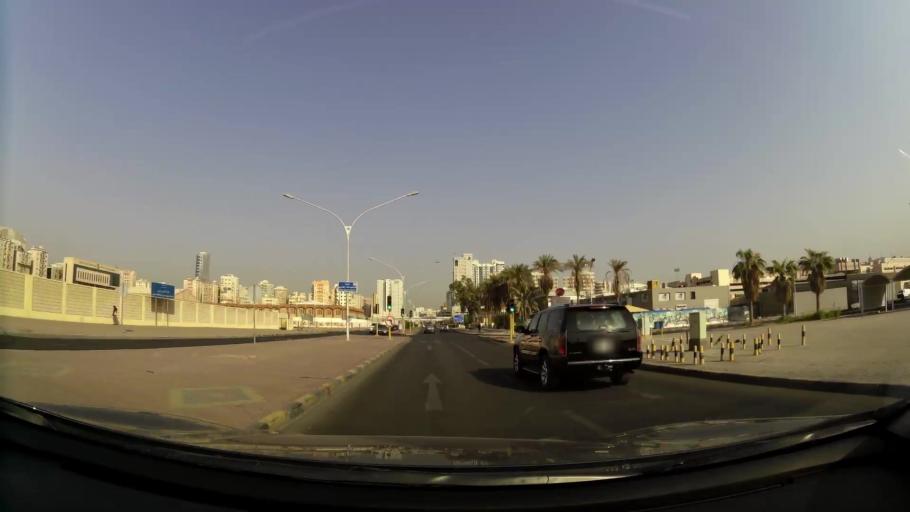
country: KW
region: Muhafazat Hawalli
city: Hawalli
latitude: 29.3248
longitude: 48.0306
